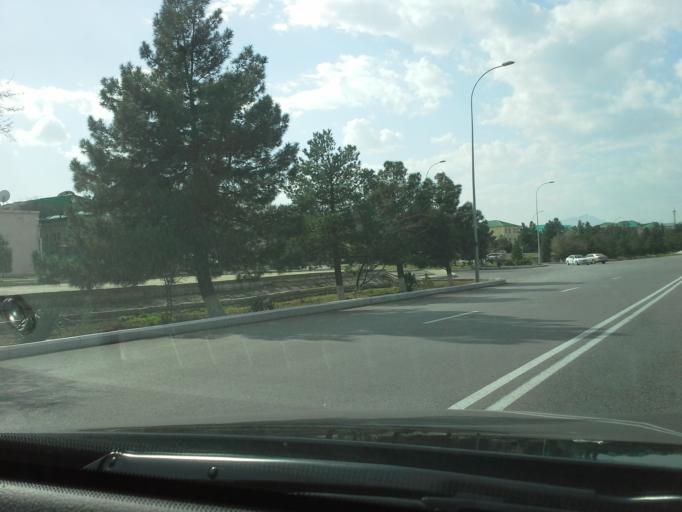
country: TM
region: Ahal
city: Ashgabat
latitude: 37.9581
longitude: 58.3212
